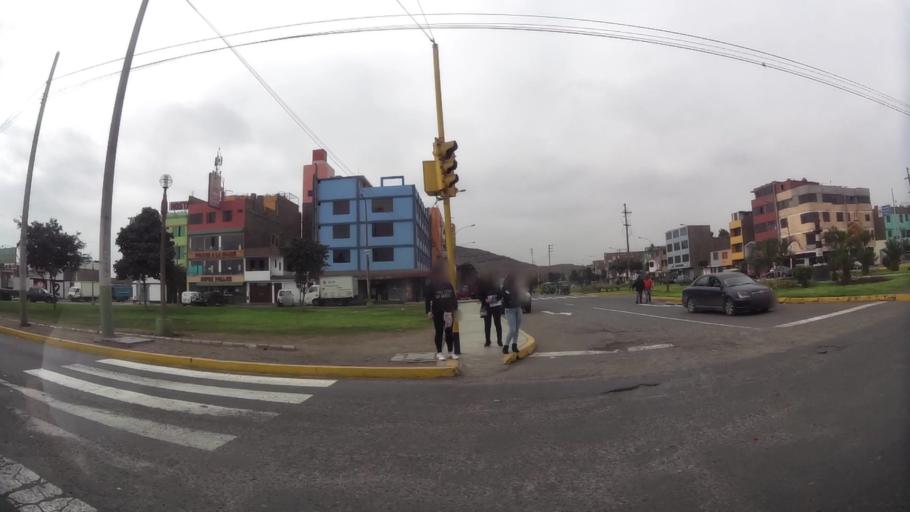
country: PE
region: Callao
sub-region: Callao
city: Callao
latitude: -11.9988
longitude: -77.1215
